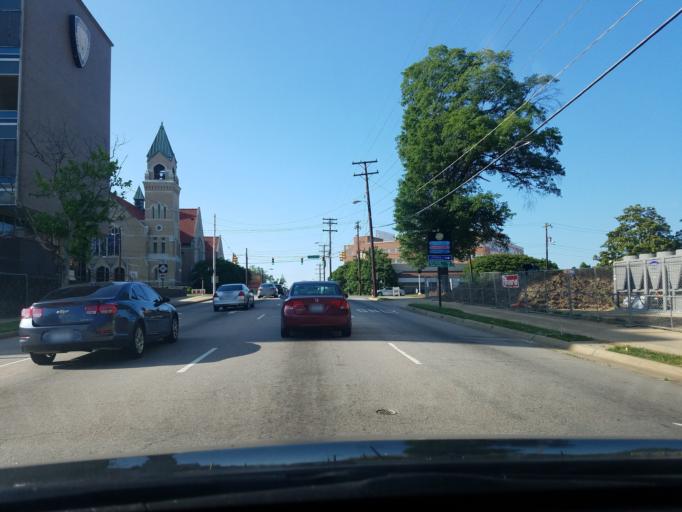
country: US
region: North Carolina
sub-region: Durham County
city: Durham
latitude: 35.9963
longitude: -78.9088
